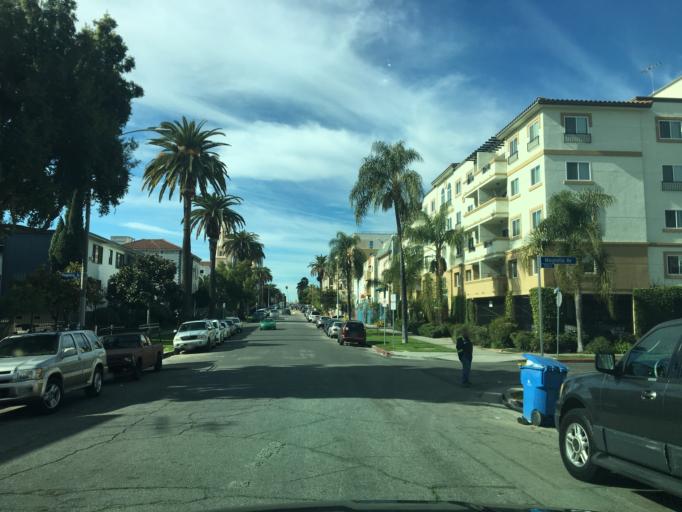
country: US
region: California
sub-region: Los Angeles County
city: Echo Park
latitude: 34.0587
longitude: -118.2859
